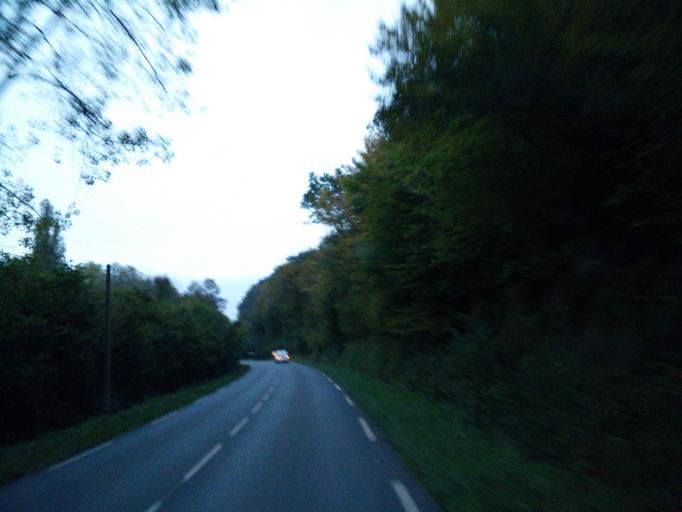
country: FR
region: Aquitaine
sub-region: Departement de la Dordogne
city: Saint-Cyprien
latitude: 44.9432
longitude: 1.0361
